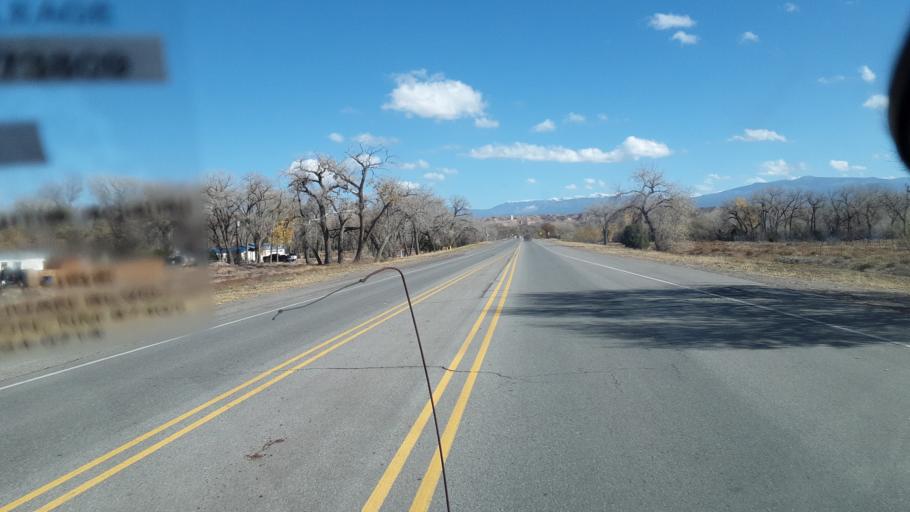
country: US
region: New Mexico
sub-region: Rio Arriba County
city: Espanola
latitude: 36.0082
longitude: -106.0776
